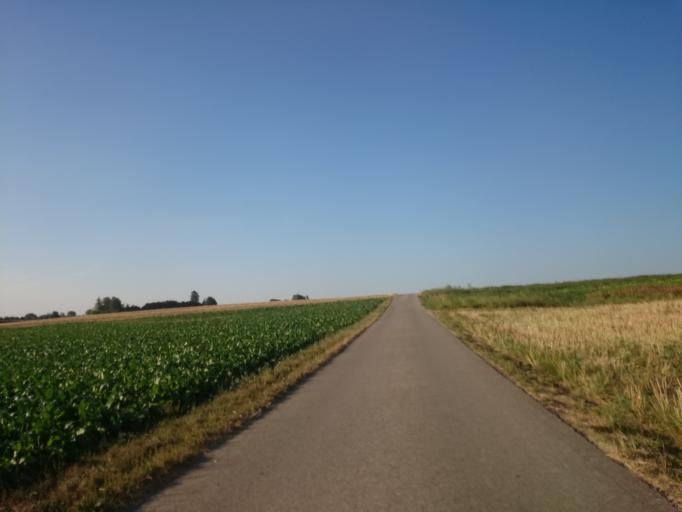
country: DE
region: Bavaria
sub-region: Swabia
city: Konigsbrunn
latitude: 48.3018
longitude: 10.8667
